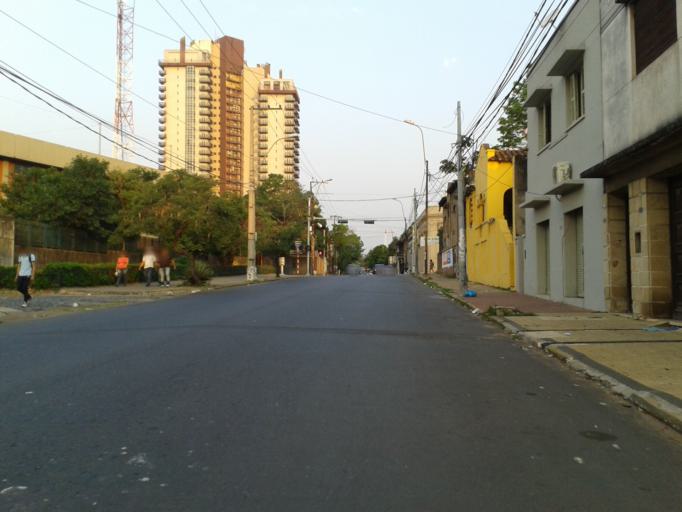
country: PY
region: Asuncion
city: Asuncion
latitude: -25.2845
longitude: -57.6251
